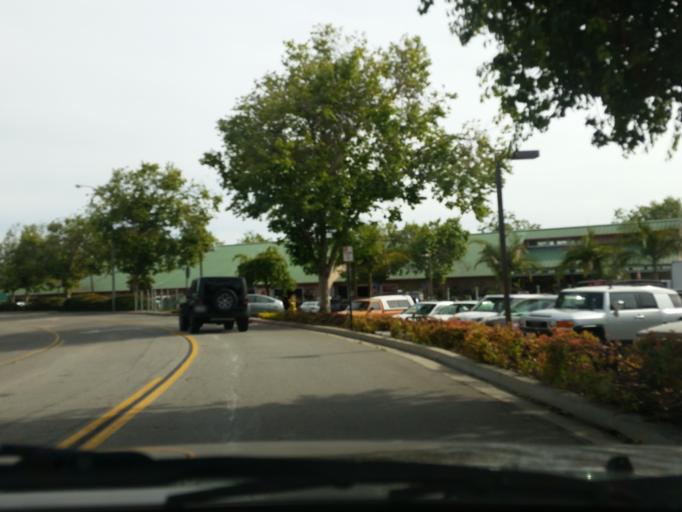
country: US
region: California
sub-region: San Luis Obispo County
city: Arroyo Grande
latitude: 35.1216
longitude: -120.5796
